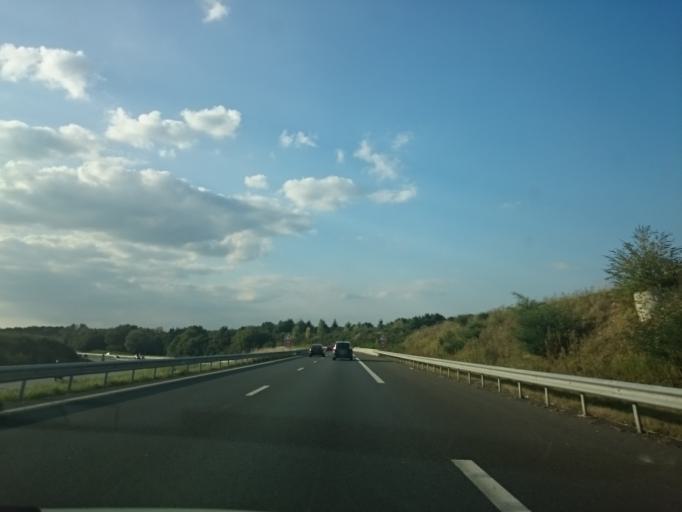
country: FR
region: Pays de la Loire
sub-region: Departement de la Loire-Atlantique
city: Sautron
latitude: 47.2536
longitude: -1.6803
